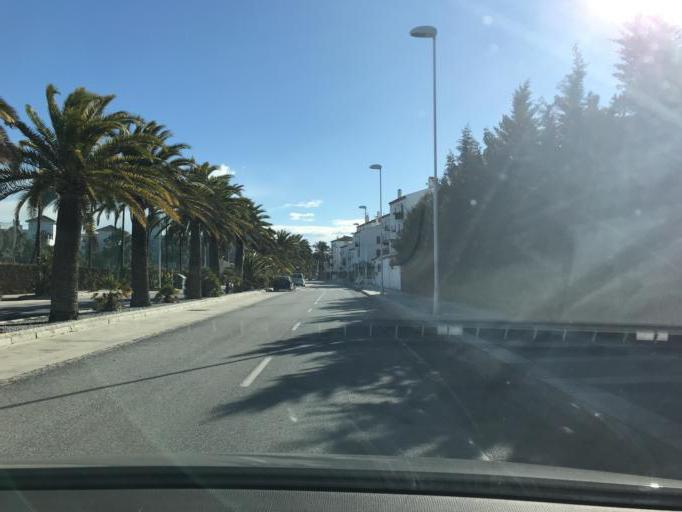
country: ES
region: Andalusia
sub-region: Provincia de Granada
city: Salobrena
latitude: 36.7205
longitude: -3.5623
